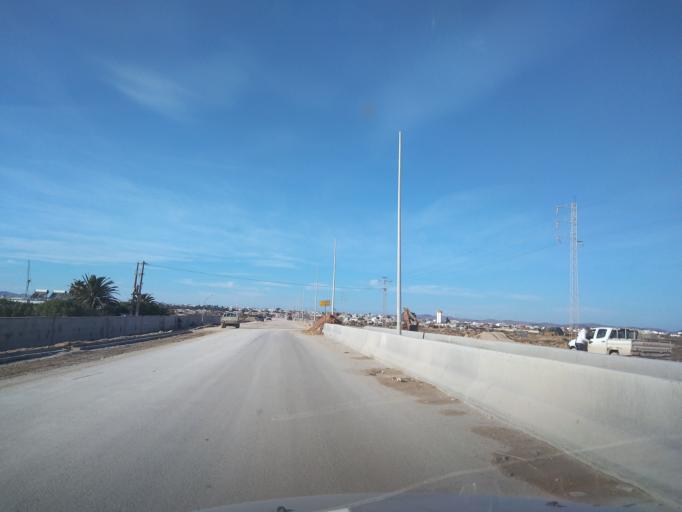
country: TN
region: Ariana
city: Qal'at al Andalus
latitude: 37.0418
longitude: 10.1298
